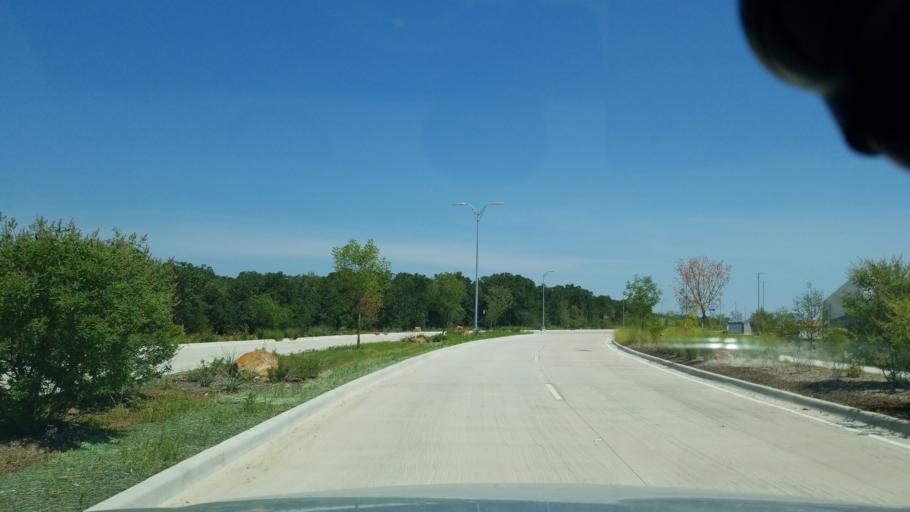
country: US
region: Texas
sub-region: Tarrant County
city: Euless
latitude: 32.8412
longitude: -97.0308
